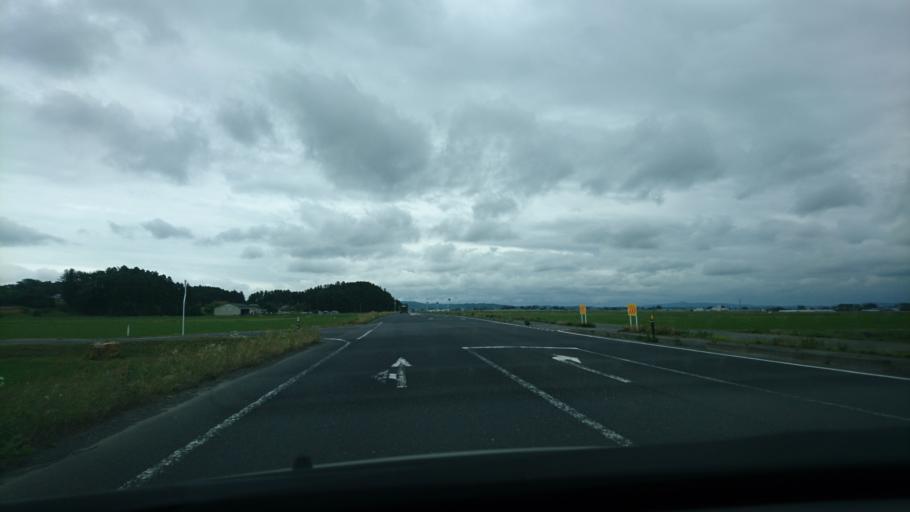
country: JP
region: Miyagi
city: Wakuya
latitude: 38.6999
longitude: 141.2603
